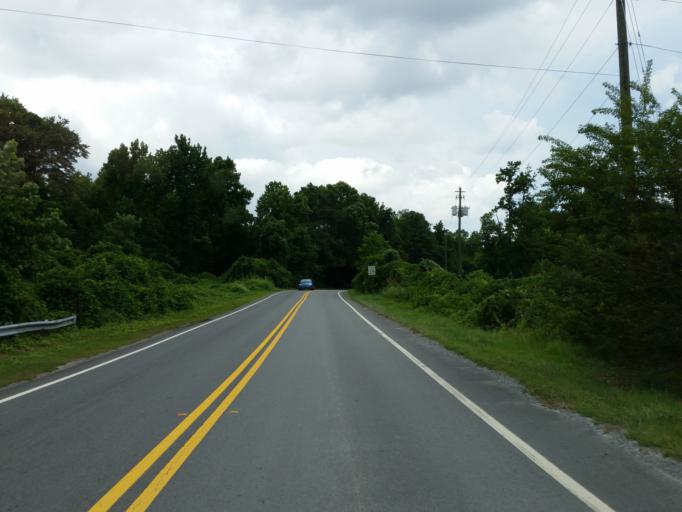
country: US
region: Georgia
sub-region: Cobb County
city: Kennesaw
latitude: 34.0200
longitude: -84.5807
